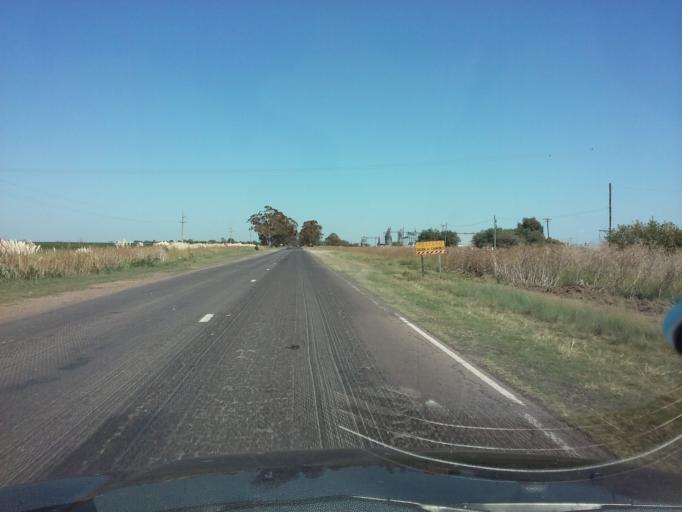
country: AR
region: La Pampa
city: General Pico
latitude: -35.6979
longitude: -63.7933
